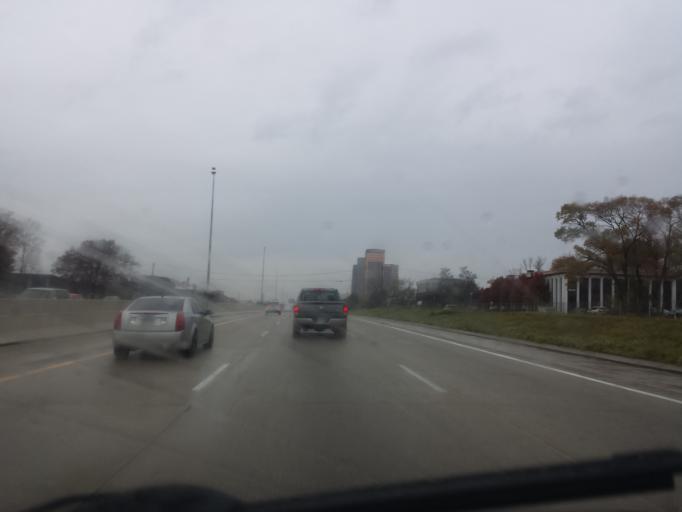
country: US
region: Michigan
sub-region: Oakland County
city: Southfield
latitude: 42.4674
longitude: -83.2341
